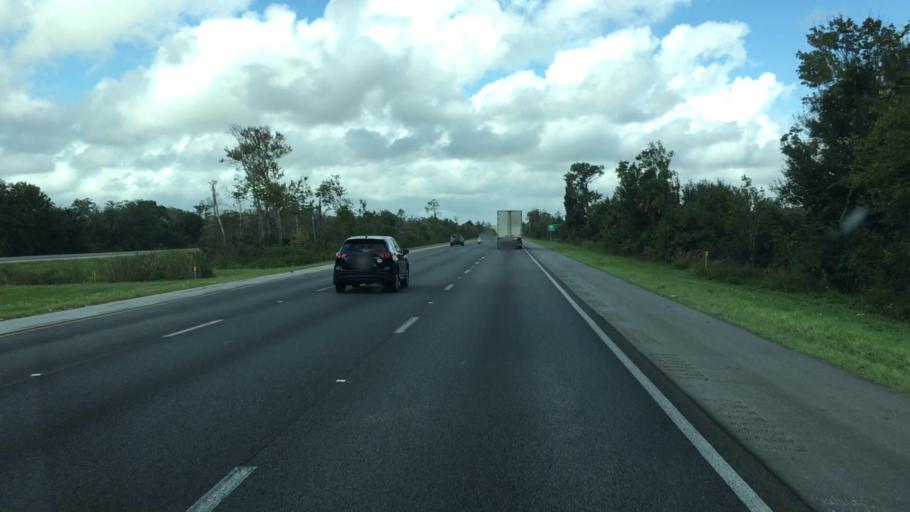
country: US
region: Florida
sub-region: Volusia County
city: Glencoe
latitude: 29.0234
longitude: -80.9945
